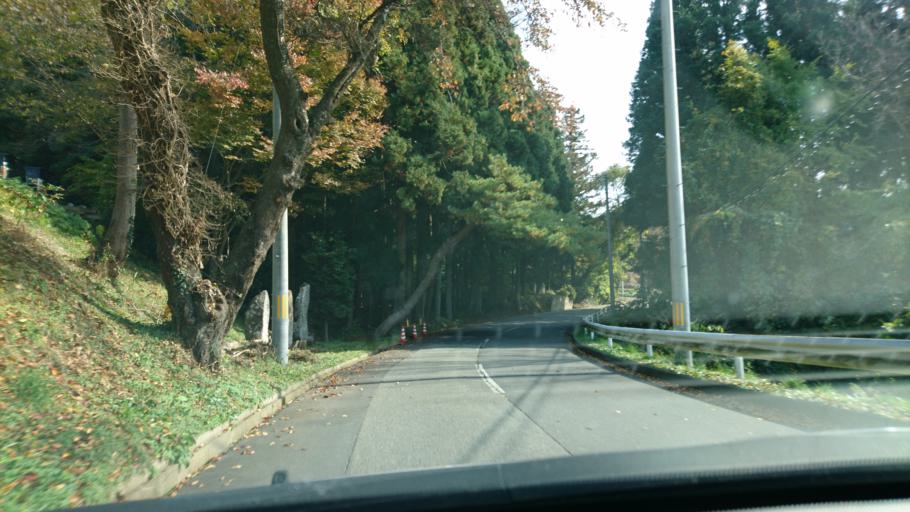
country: JP
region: Iwate
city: Ichinoseki
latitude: 38.9774
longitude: 141.1768
